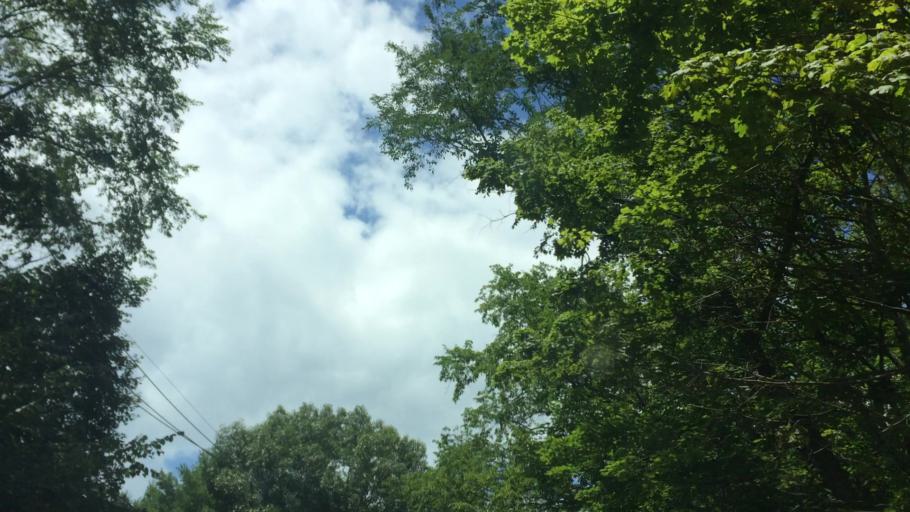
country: US
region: Massachusetts
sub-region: Middlesex County
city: Maynard
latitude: 42.4223
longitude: -71.4454
